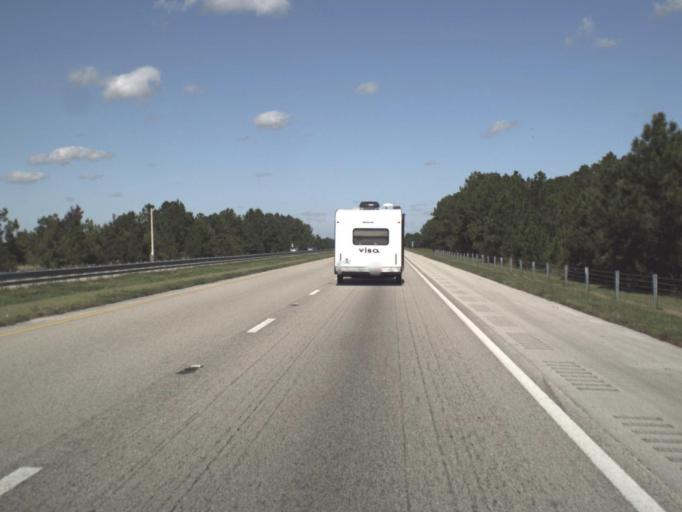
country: US
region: Florida
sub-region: Brevard County
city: June Park
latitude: 27.8984
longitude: -81.0419
